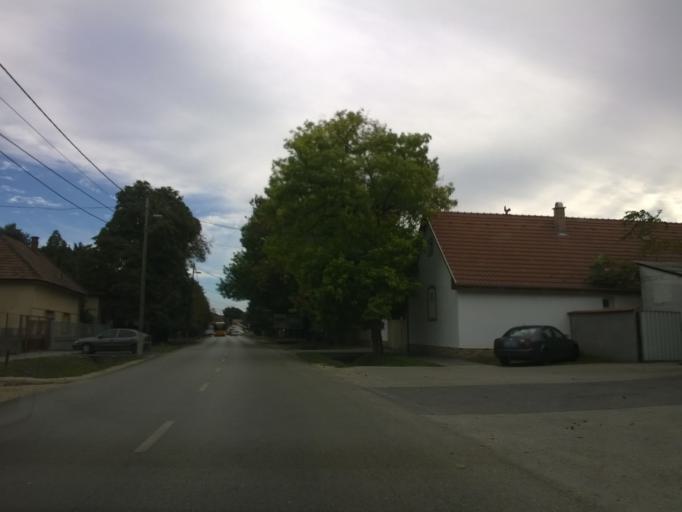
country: HU
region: Pest
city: Szigetszentmiklos
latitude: 47.3509
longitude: 19.0413
